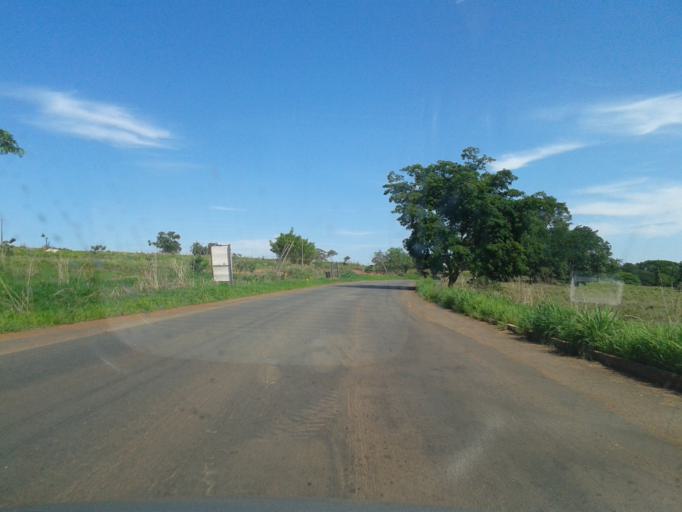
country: BR
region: Goias
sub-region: Piracanjuba
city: Piracanjuba
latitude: -17.2298
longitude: -48.7128
